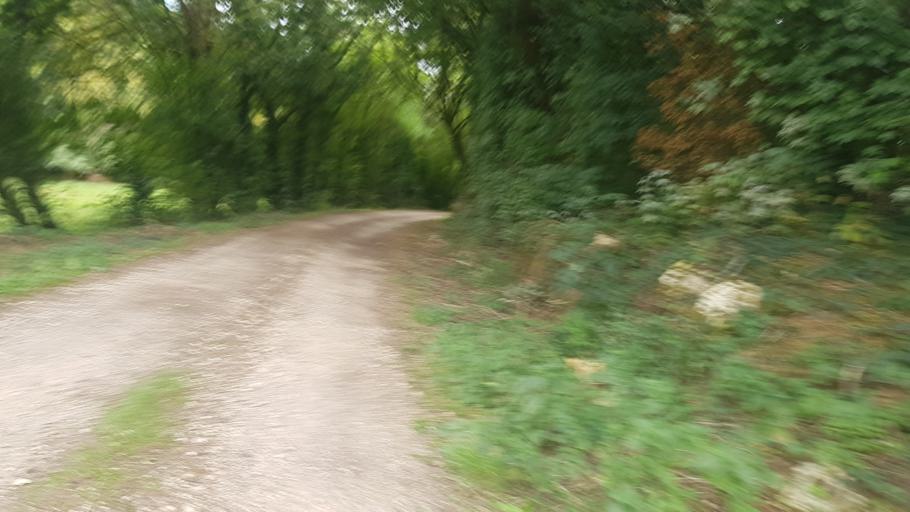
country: FR
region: Poitou-Charentes
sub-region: Departement des Deux-Sevres
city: Vouille
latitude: 46.3146
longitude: -0.3420
